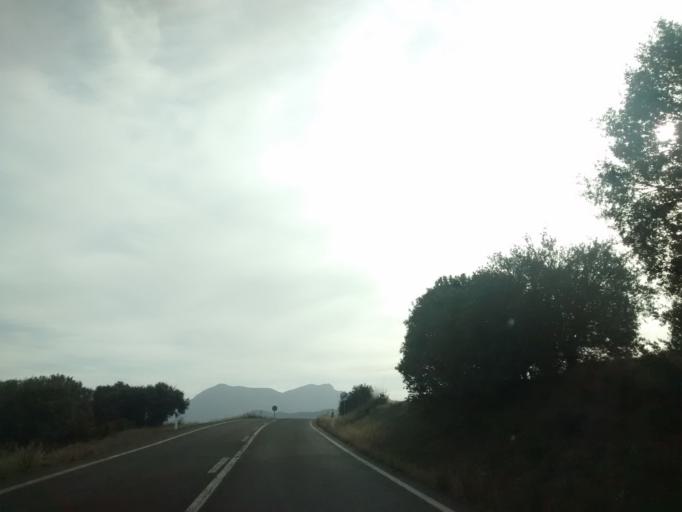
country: ES
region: Aragon
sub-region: Provincia de Huesca
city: Bailo
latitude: 42.5810
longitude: -0.8275
